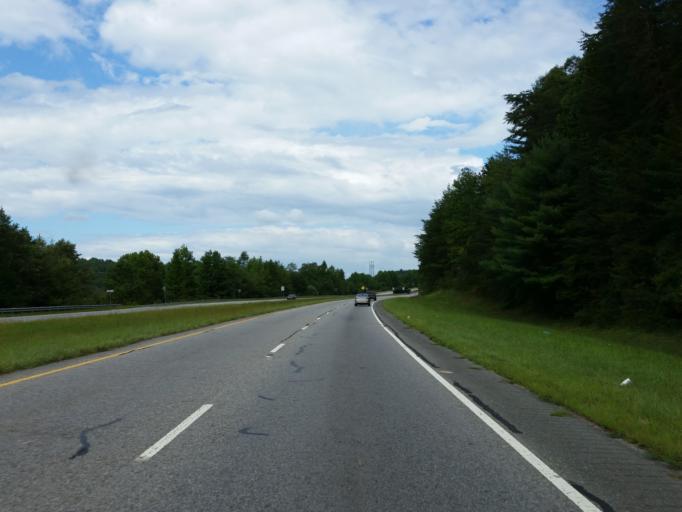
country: US
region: Georgia
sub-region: Fannin County
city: Blue Ridge
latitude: 34.8863
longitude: -84.2905
